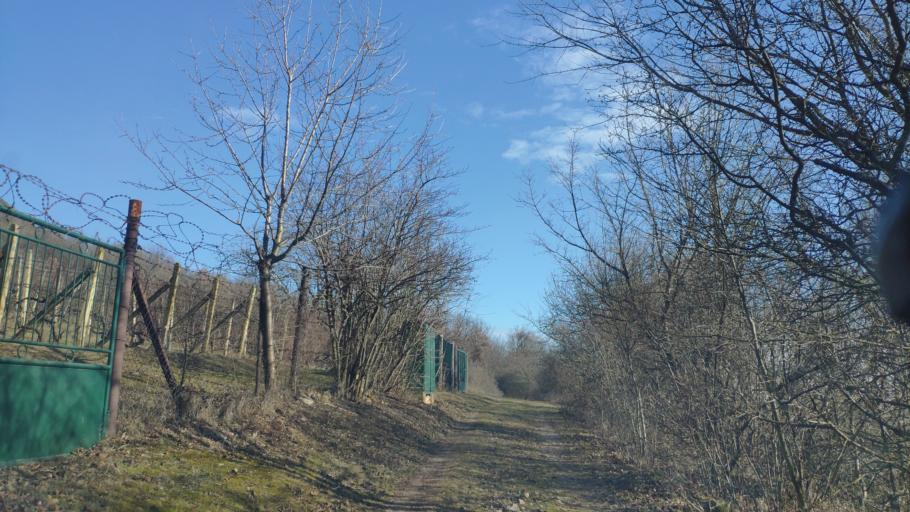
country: SK
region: Kosicky
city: Roznava
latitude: 48.6023
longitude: 20.7200
